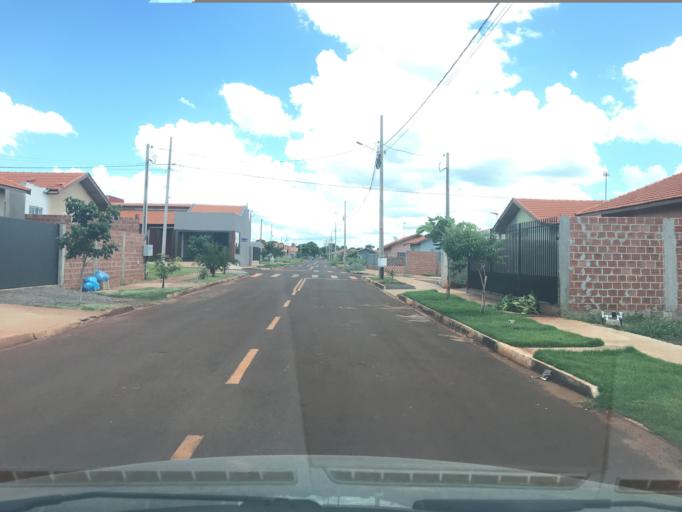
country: BR
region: Parana
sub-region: Palotina
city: Palotina
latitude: -24.2651
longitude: -53.8464
